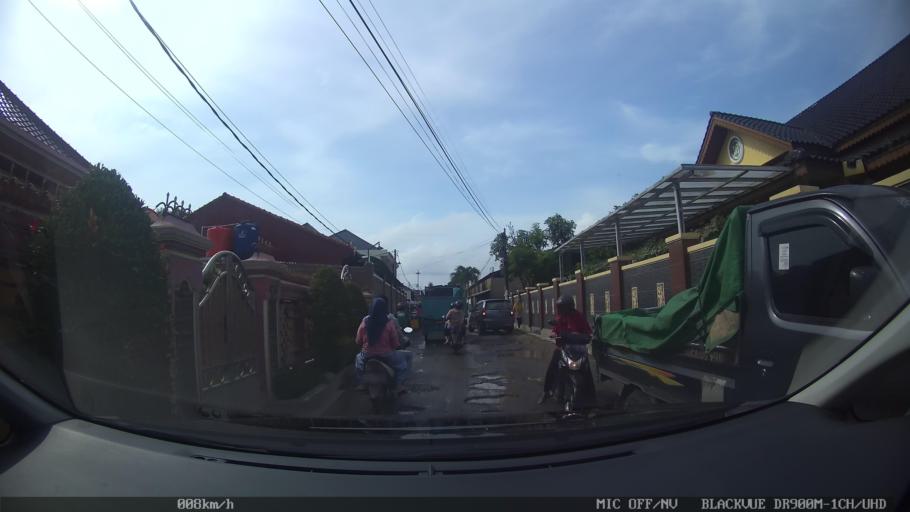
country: ID
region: Lampung
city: Kedaton
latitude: -5.3835
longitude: 105.2950
